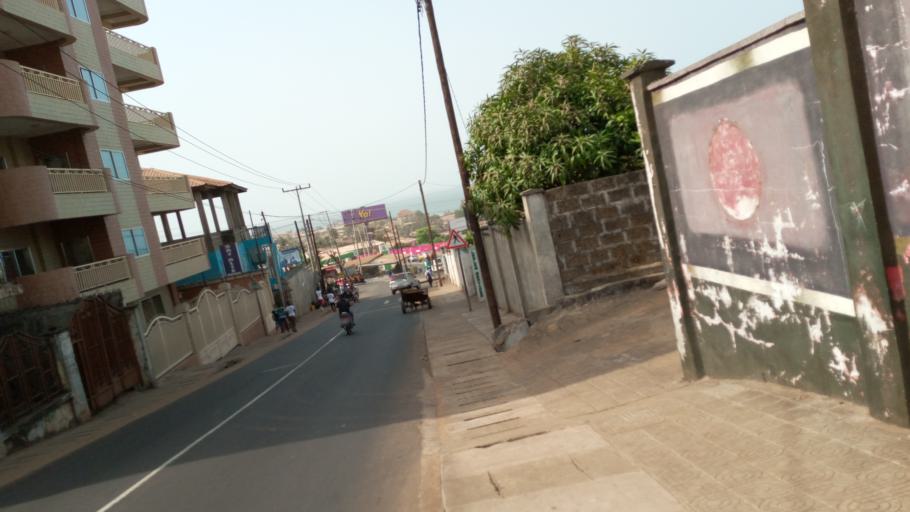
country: SL
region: Western Area
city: Freetown
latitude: 8.4823
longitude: -13.2589
